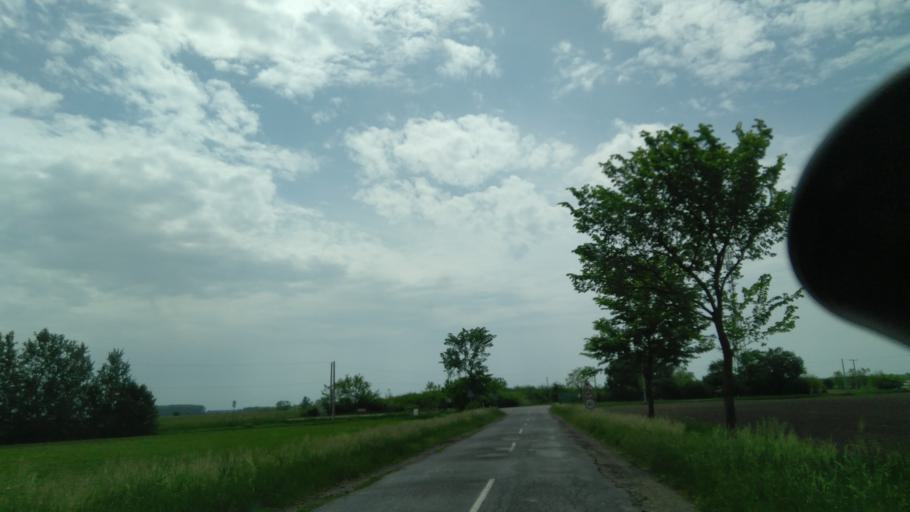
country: RO
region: Bihor
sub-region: Comuna Sannicolau-Roman
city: Sannicolau Roman
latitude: 47.0001
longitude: 21.6207
